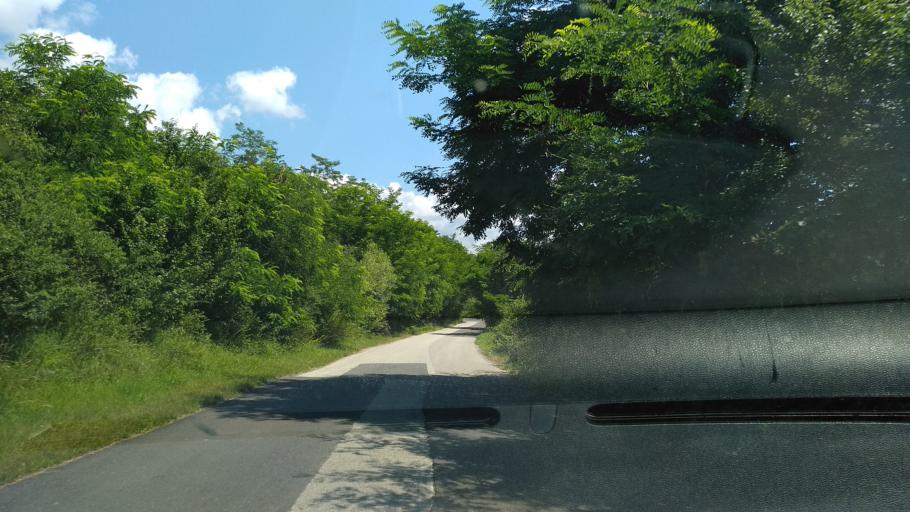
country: RO
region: Hunedoara
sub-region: Comuna Bosorod
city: Bosorod
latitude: 45.6991
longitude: 23.0889
